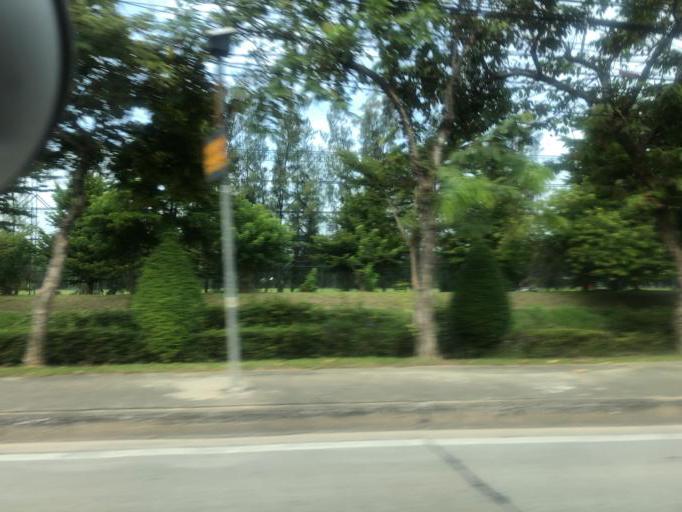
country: TH
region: Bangkok
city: Bang Khen
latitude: 13.8685
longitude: 100.6069
